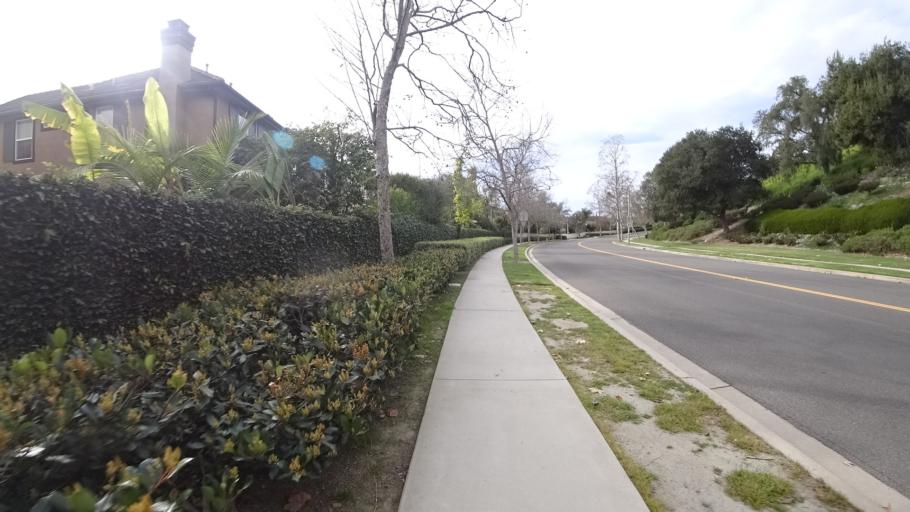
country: US
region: California
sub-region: Orange County
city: Aliso Viejo
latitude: 33.5619
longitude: -117.7391
